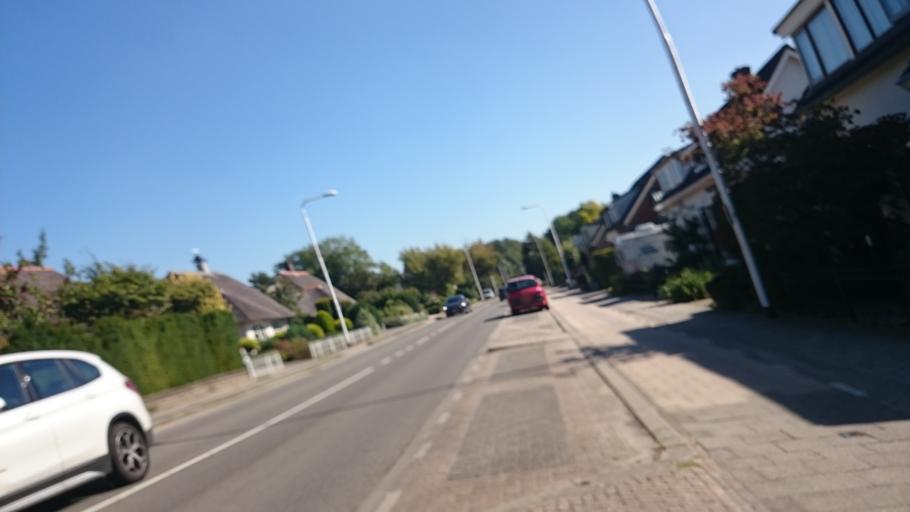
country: NL
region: Gelderland
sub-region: Gemeente Overbetuwe
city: Elst
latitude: 51.8950
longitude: 5.9056
